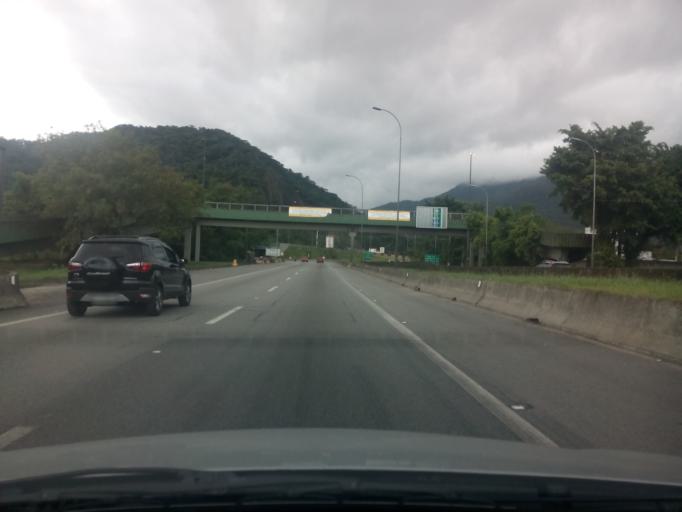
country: BR
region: Sao Paulo
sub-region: Cubatao
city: Cubatao
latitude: -23.8875
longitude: -46.4377
